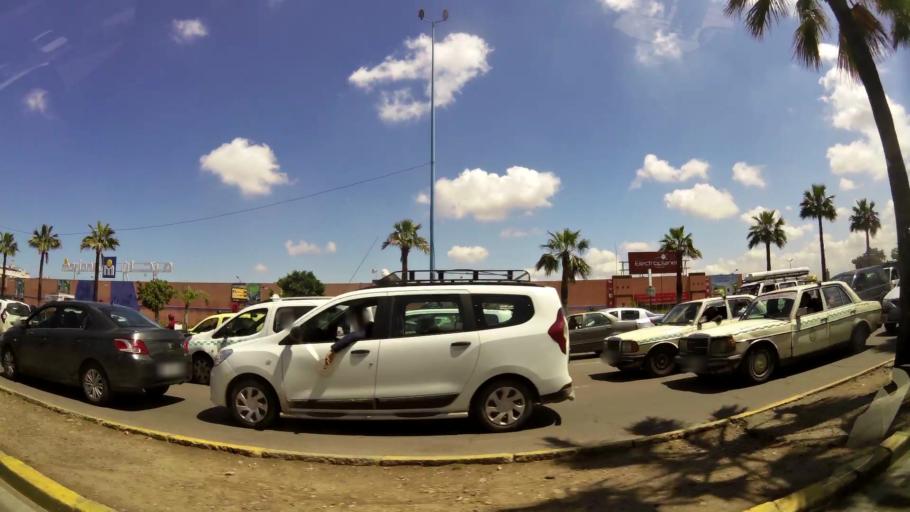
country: MA
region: Grand Casablanca
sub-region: Casablanca
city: Casablanca
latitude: 33.5612
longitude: -7.5948
